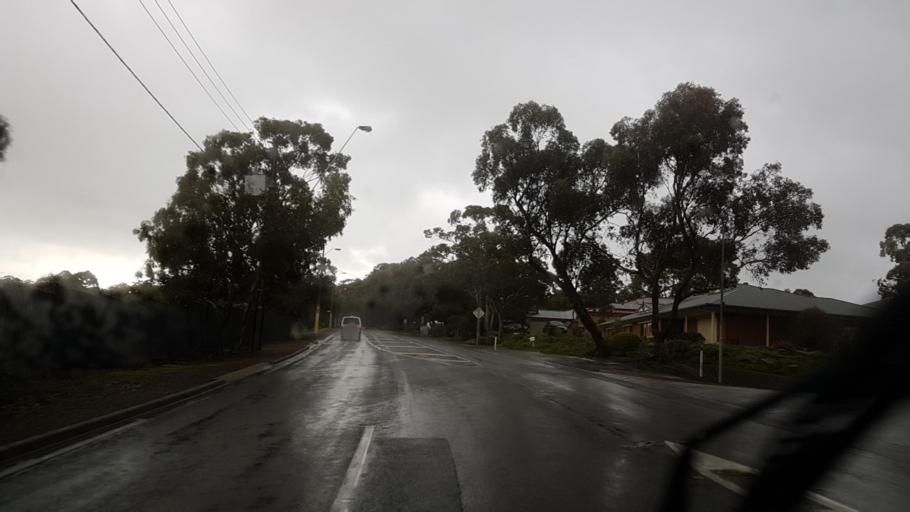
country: AU
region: South Australia
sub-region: Onkaparinga
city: Craigburn Farm
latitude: -35.0873
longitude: 138.5887
